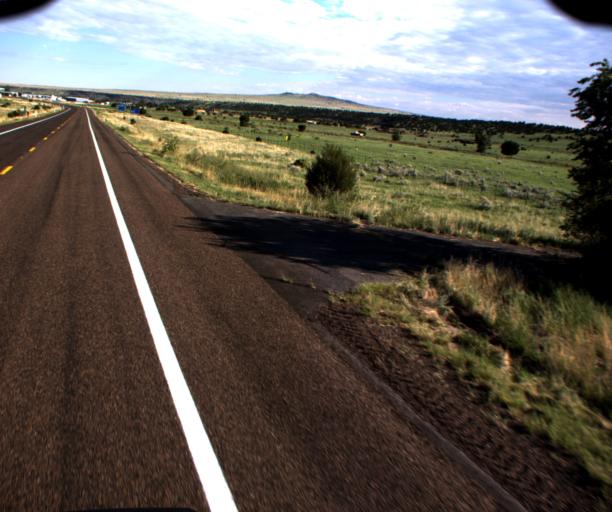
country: US
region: Arizona
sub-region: Apache County
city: Eagar
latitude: 34.1023
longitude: -109.2460
